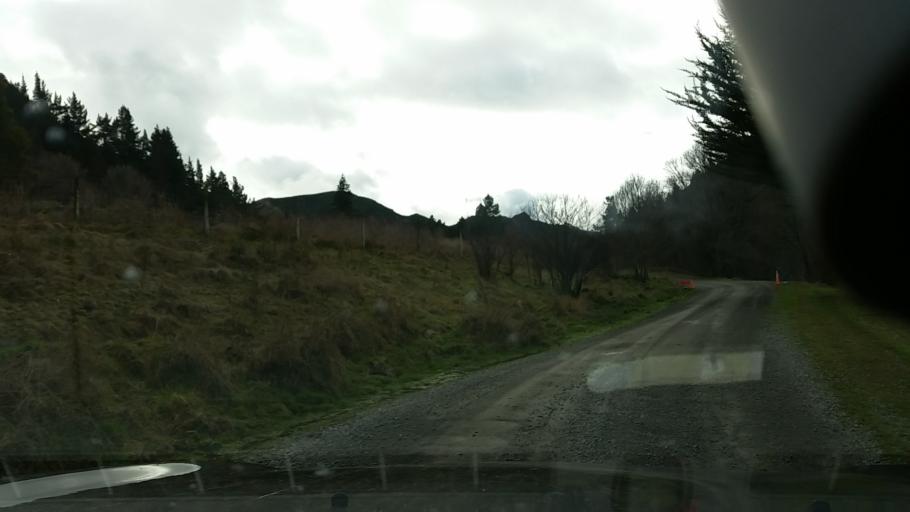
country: NZ
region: Tasman
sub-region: Tasman District
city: Richmond
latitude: -41.7286
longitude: 173.4696
